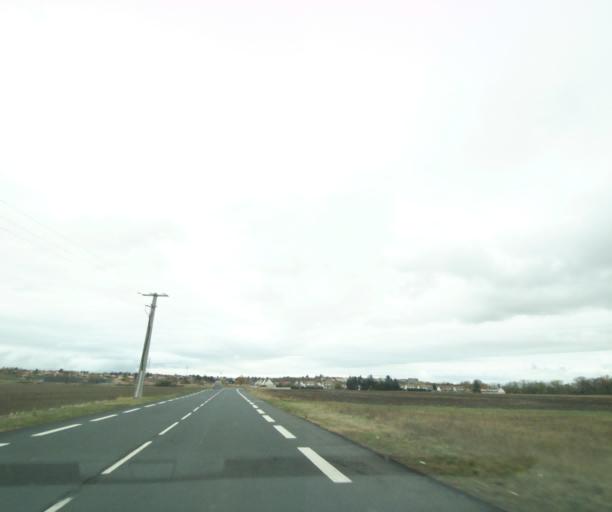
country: FR
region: Auvergne
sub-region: Departement du Puy-de-Dome
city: Dallet
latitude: 45.7837
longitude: 3.2379
